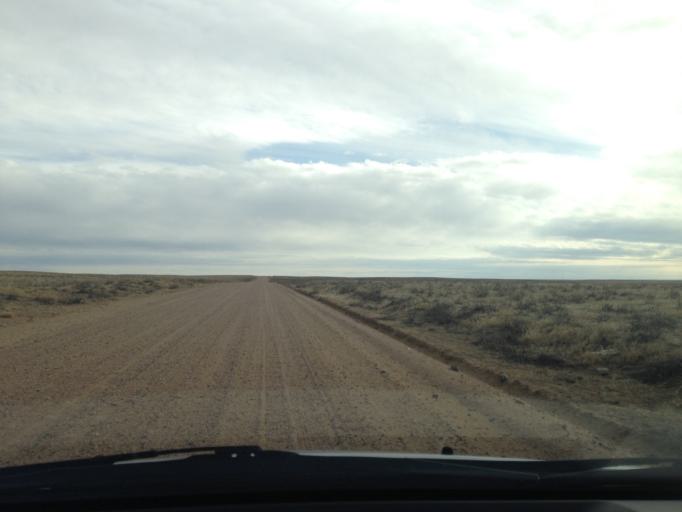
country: US
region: Colorado
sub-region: Weld County
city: Keenesburg
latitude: 40.2429
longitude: -104.2068
